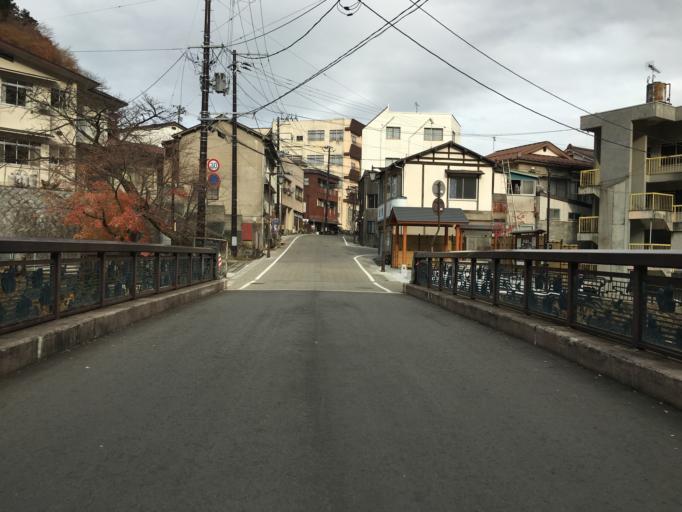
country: JP
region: Fukushima
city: Nihommatsu
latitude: 37.6826
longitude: 140.3257
